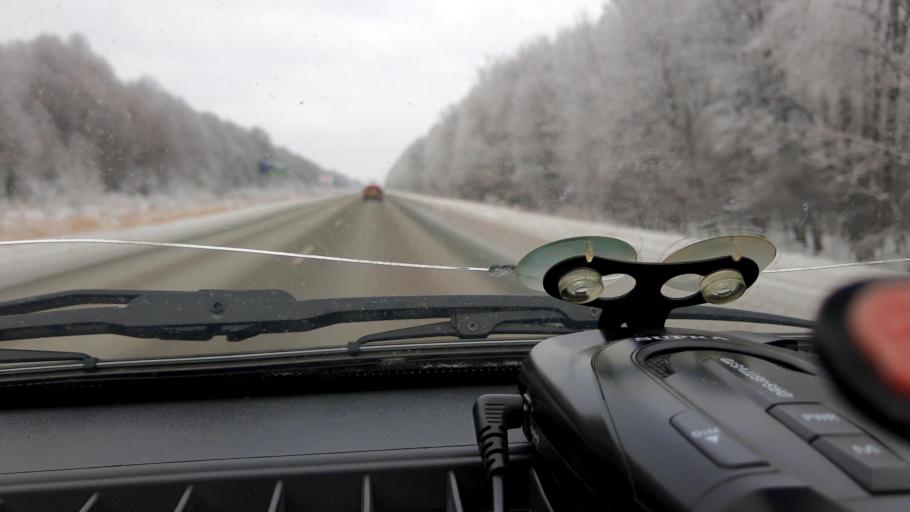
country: RU
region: Bashkortostan
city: Blagoveshchensk
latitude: 54.9558
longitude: 56.0793
